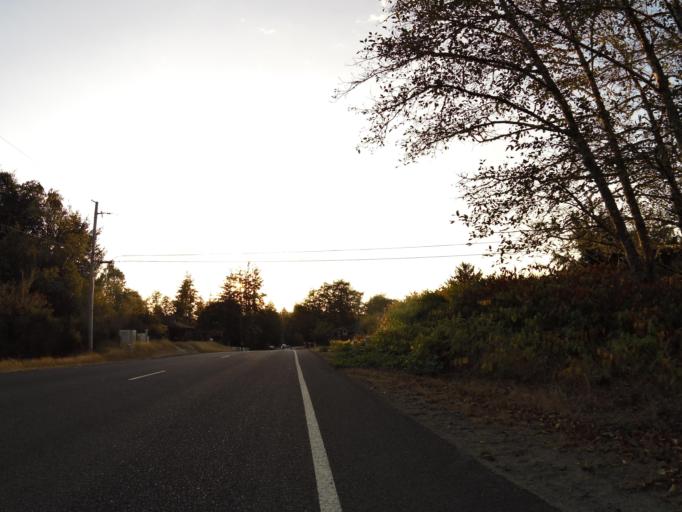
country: US
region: Oregon
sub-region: Clatsop County
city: Warrenton
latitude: 46.1579
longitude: -123.9399
